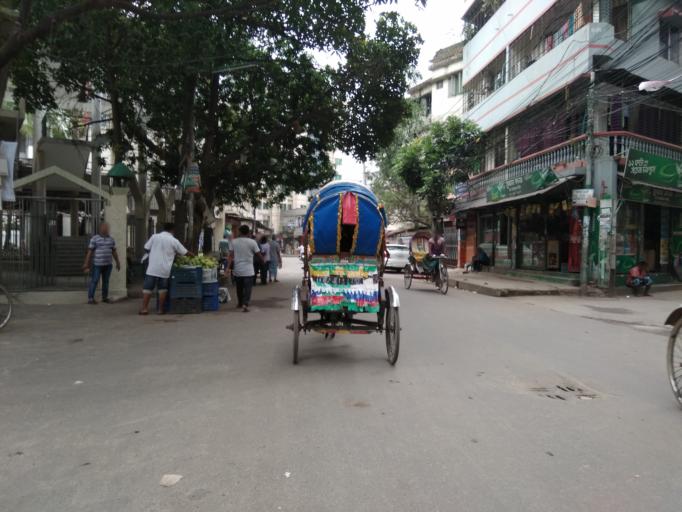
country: BD
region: Dhaka
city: Tungi
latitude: 23.8229
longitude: 90.3626
